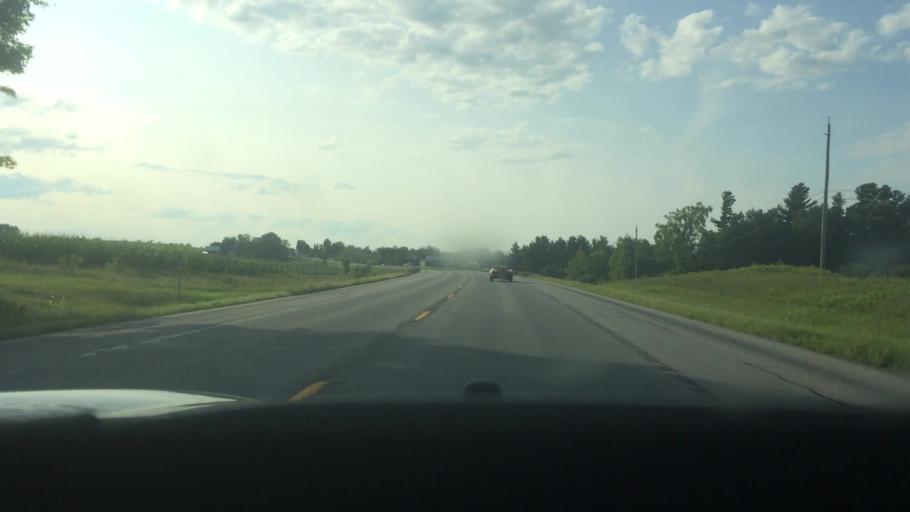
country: US
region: New York
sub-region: St. Lawrence County
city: Canton
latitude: 44.6289
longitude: -75.2402
